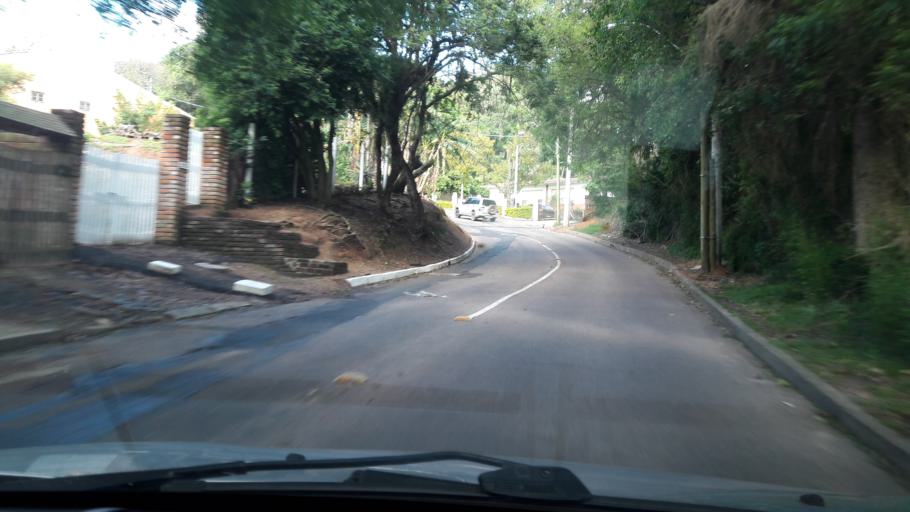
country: BR
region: Rio Grande do Sul
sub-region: Porto Alegre
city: Porto Alegre
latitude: -30.0852
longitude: -51.2006
